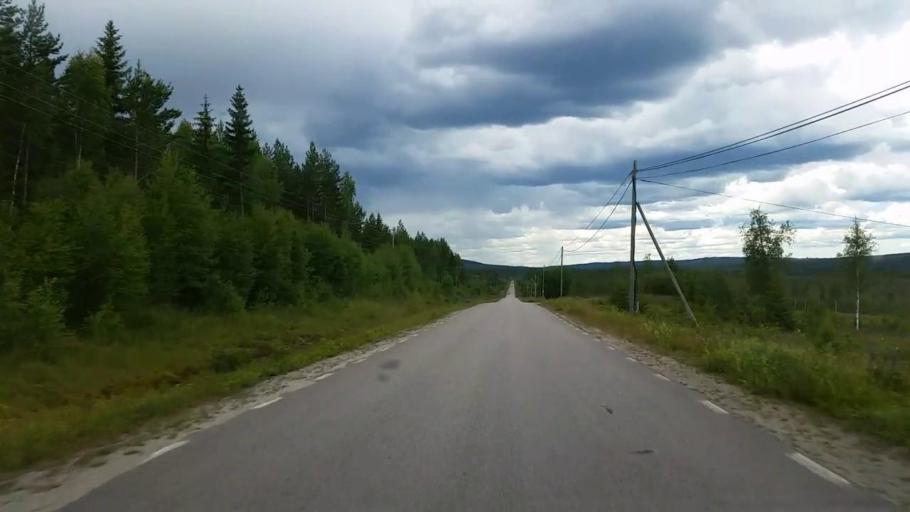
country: SE
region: Gaevleborg
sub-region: Ovanakers Kommun
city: Edsbyn
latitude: 61.4368
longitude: 15.8944
